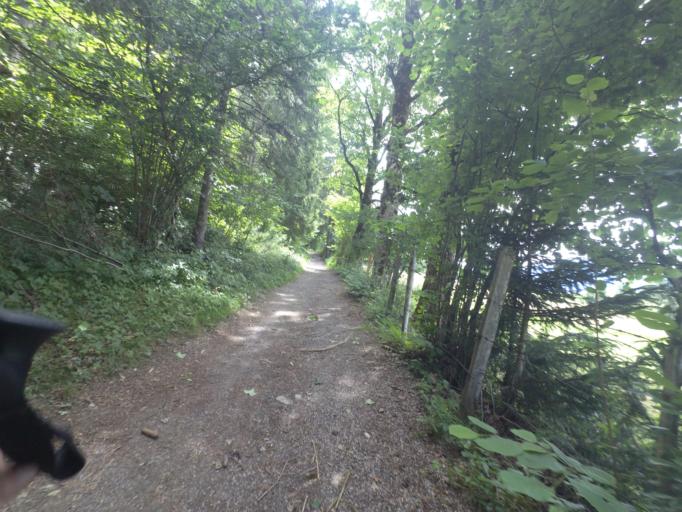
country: AT
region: Salzburg
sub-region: Politischer Bezirk Zell am See
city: Saalfelden am Steinernen Meer
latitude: 47.4433
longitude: 12.8564
